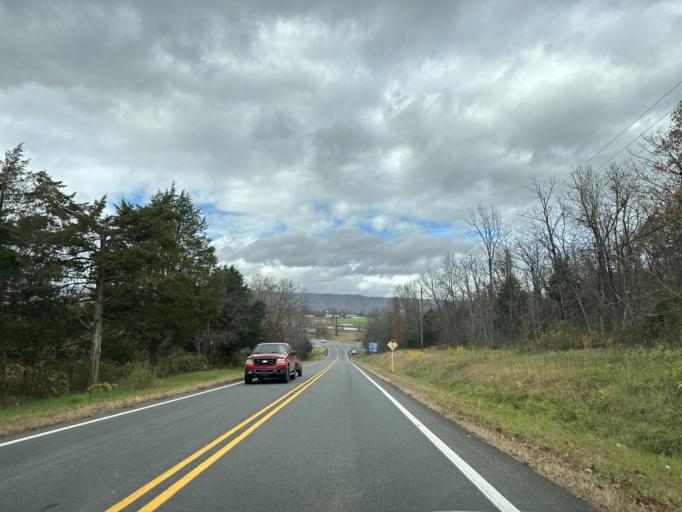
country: US
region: Virginia
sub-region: Shenandoah County
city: Strasburg
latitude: 38.9624
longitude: -78.4341
